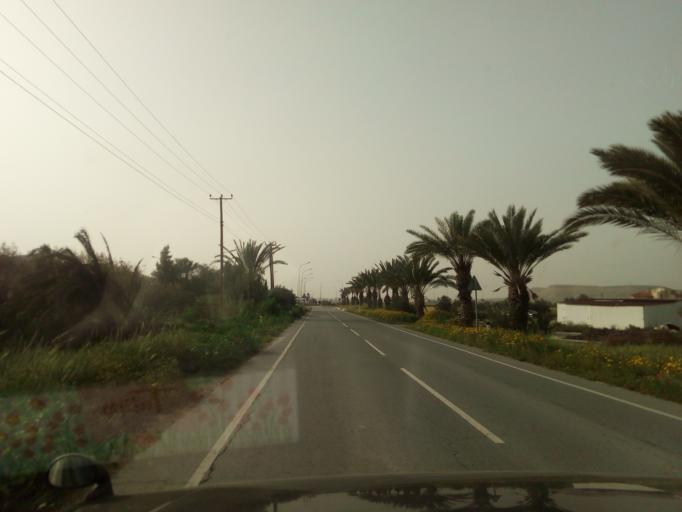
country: CY
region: Larnaka
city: Athienou
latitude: 35.0576
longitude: 33.5253
